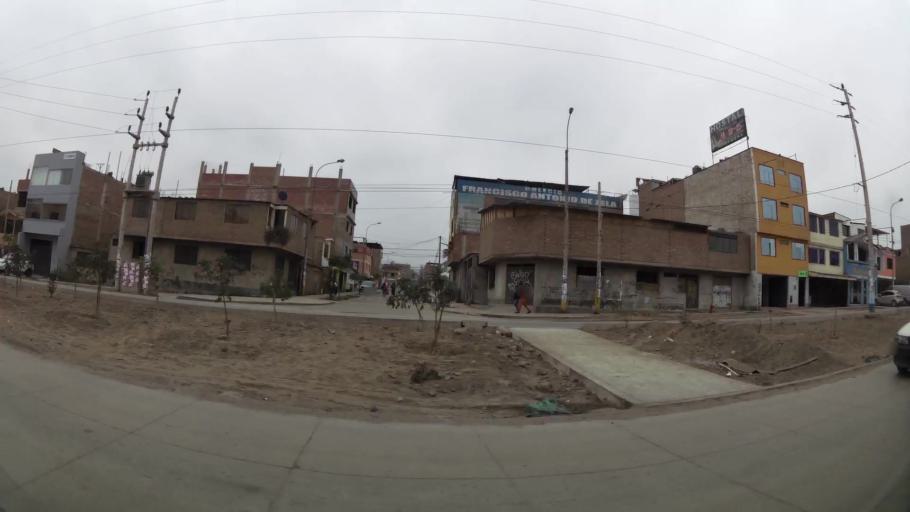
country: PE
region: Lima
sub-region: Lima
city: Surco
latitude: -12.1994
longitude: -76.9567
